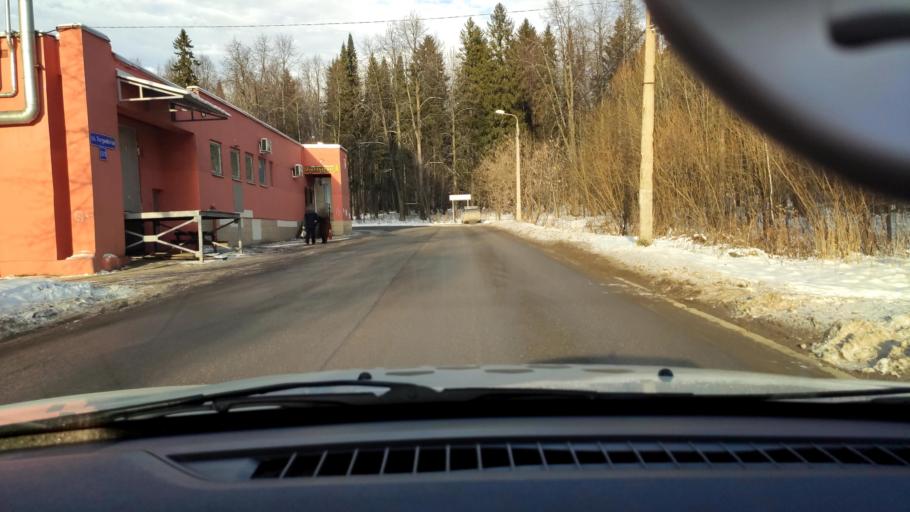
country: RU
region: Perm
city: Perm
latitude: 58.0883
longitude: 56.4124
